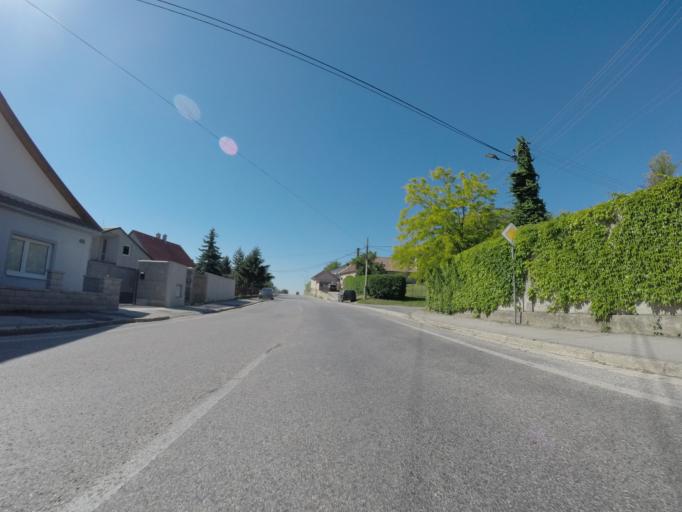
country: SK
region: Trnavsky
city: Hlohovec
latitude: 48.3883
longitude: 17.7968
